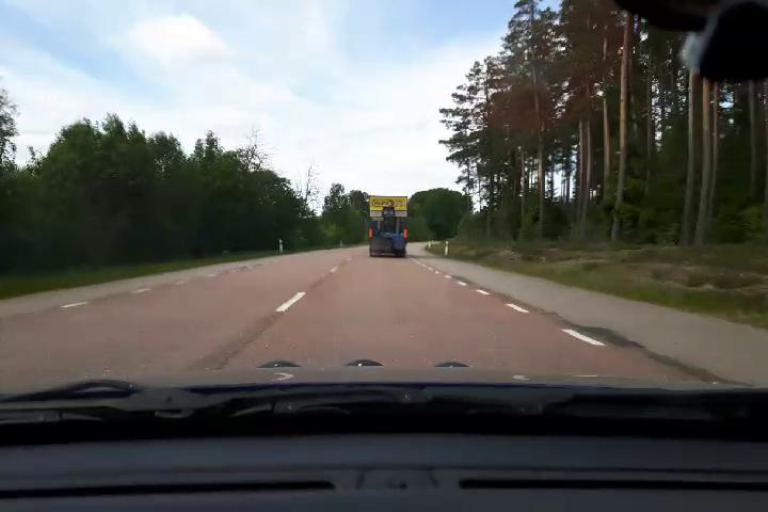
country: SE
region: Uppsala
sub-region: Osthammars Kommun
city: Bjorklinge
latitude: 60.1483
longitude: 17.4957
